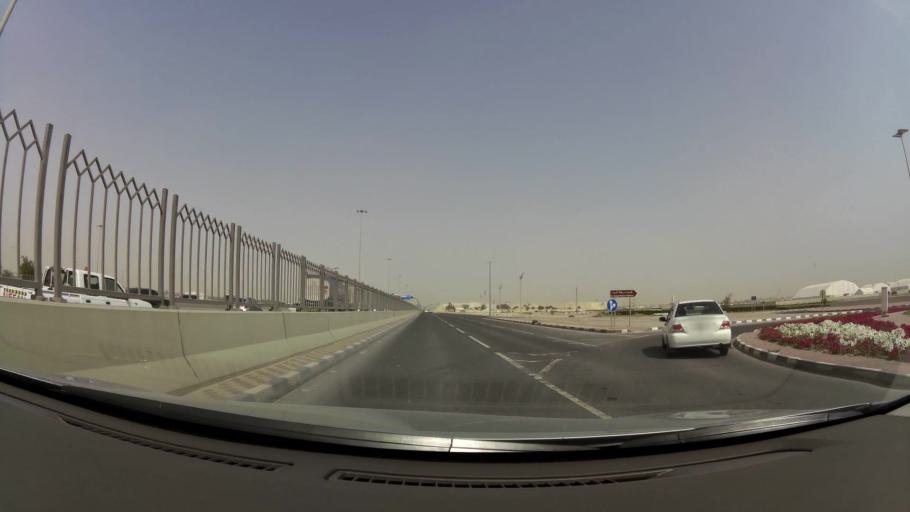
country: QA
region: Baladiyat ad Dawhah
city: Doha
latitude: 25.2795
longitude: 51.4867
